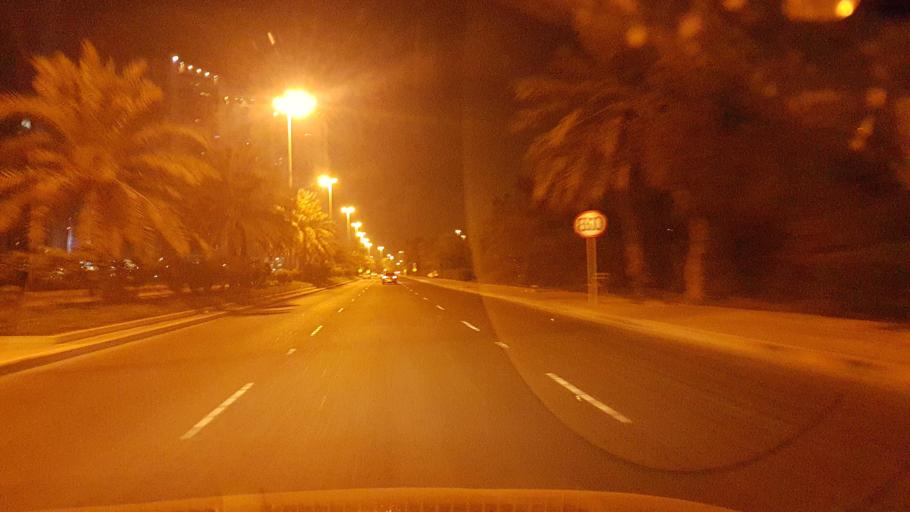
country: BH
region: Manama
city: Jidd Hafs
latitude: 26.2248
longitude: 50.5619
